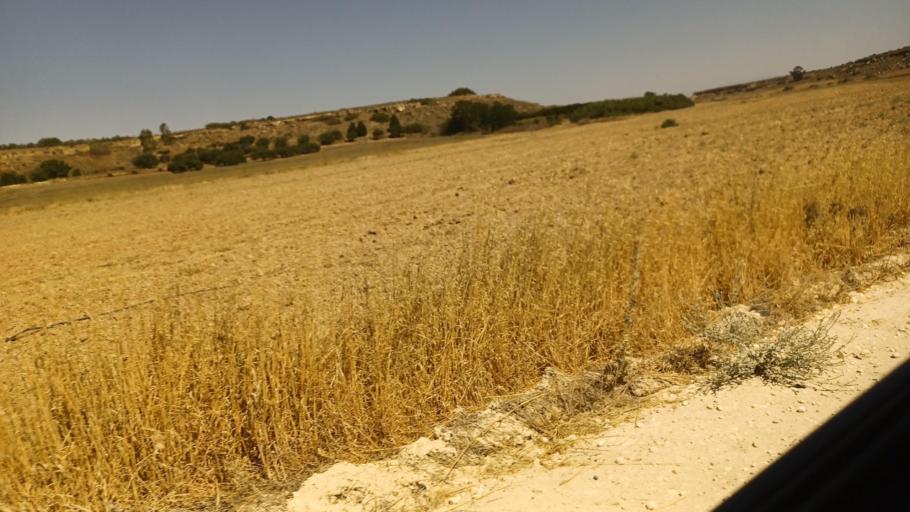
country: CY
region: Ammochostos
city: Acheritou
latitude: 35.0955
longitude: 33.8743
